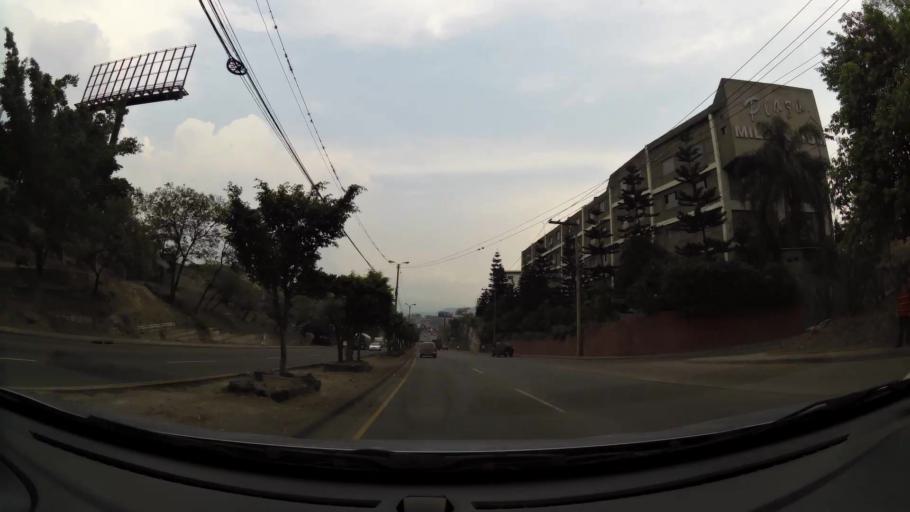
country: HN
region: Francisco Morazan
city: Tegucigalpa
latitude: 14.0781
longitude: -87.2159
